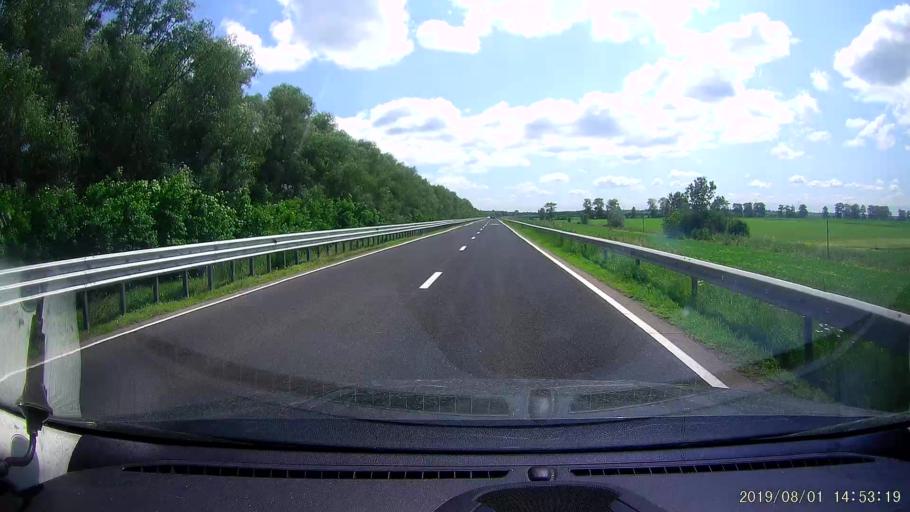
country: RO
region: Braila
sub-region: Municipiul Braila
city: Braila
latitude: 45.3381
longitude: 28.0045
